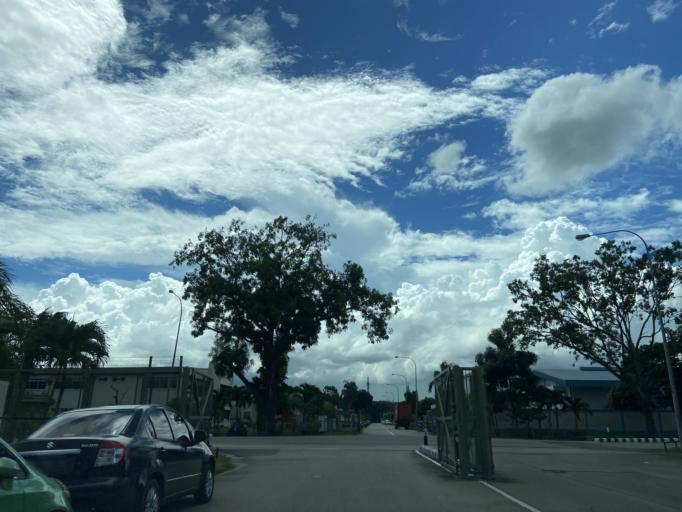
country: SG
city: Singapore
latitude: 1.0623
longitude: 104.0306
